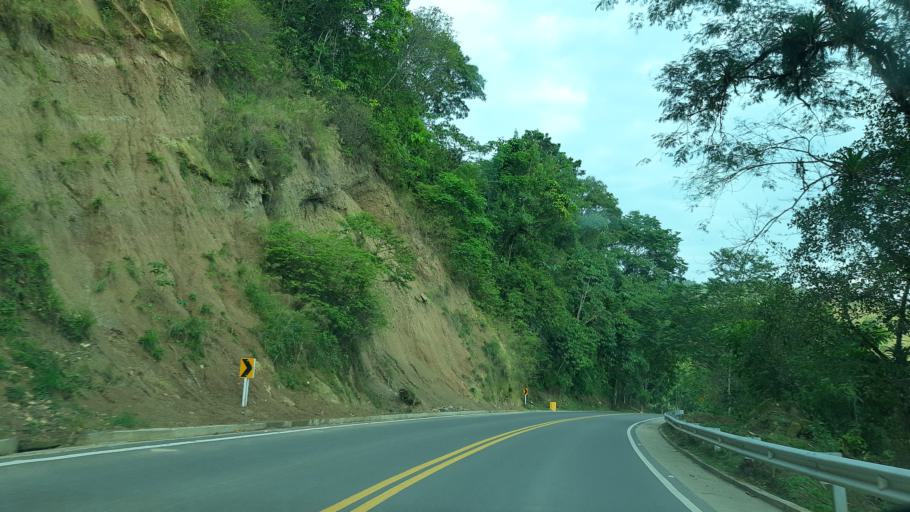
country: CO
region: Boyaca
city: San Luis de Gaceno
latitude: 4.8341
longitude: -73.1282
